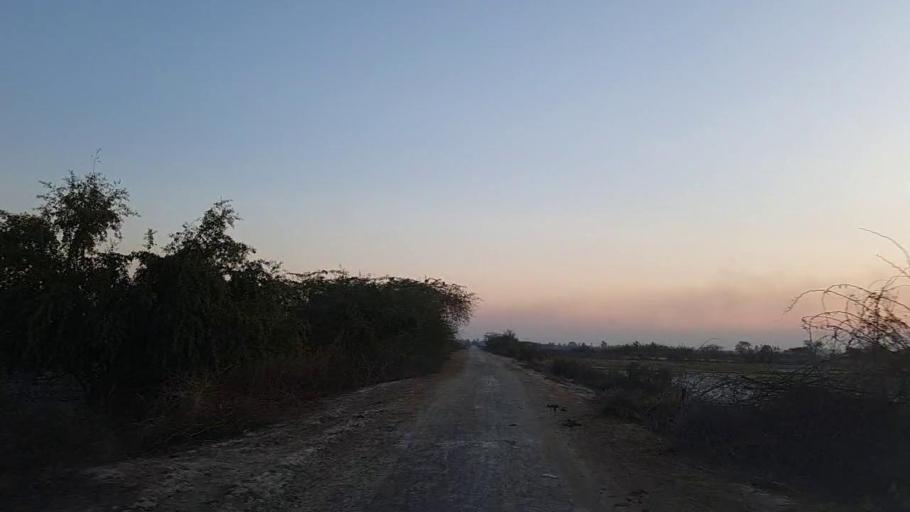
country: PK
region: Sindh
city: Bandhi
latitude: 26.5955
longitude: 68.3361
